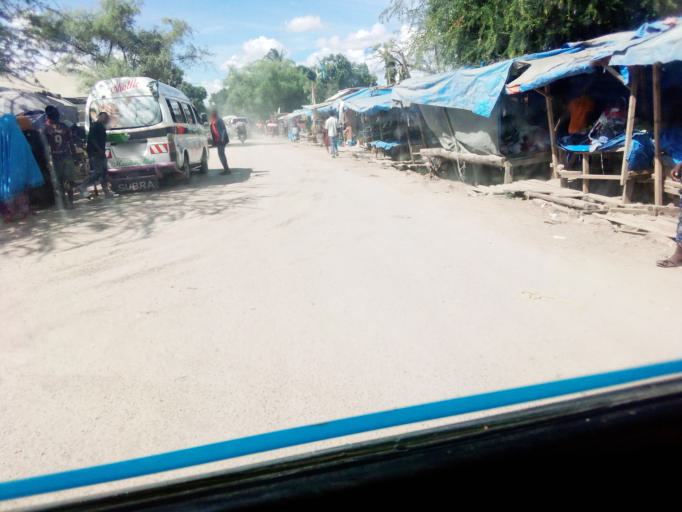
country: TZ
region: Dodoma
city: Dodoma
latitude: -6.1768
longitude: 35.7539
